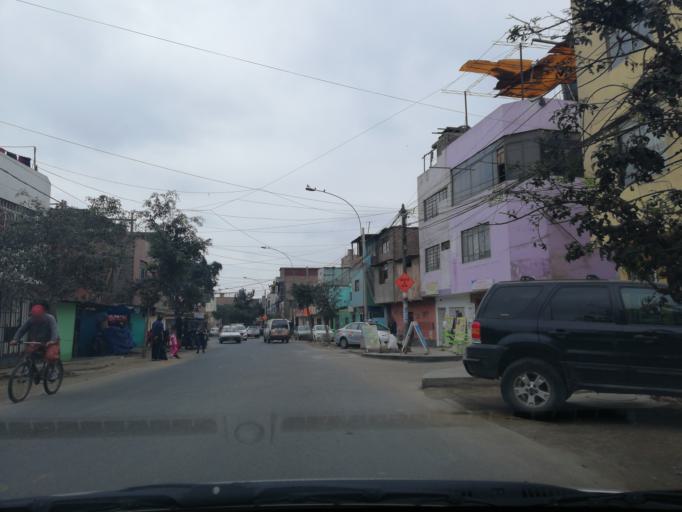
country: PE
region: Lima
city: Lima
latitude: -12.0380
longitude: -77.0485
